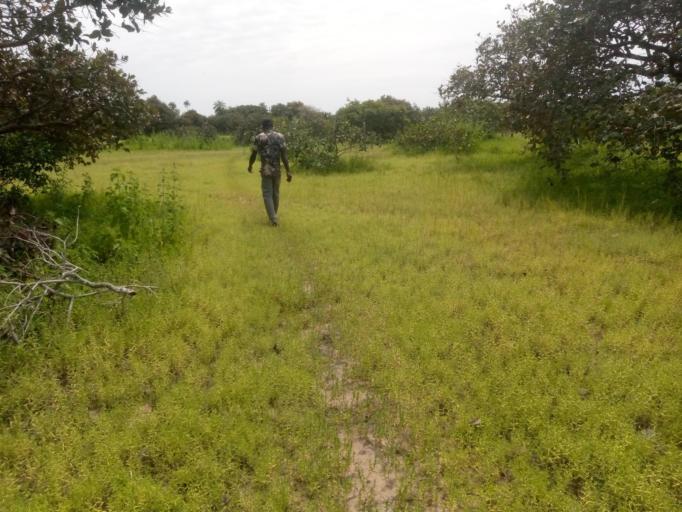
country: GM
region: Western
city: Gunjur
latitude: 13.0512
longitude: -16.7351
